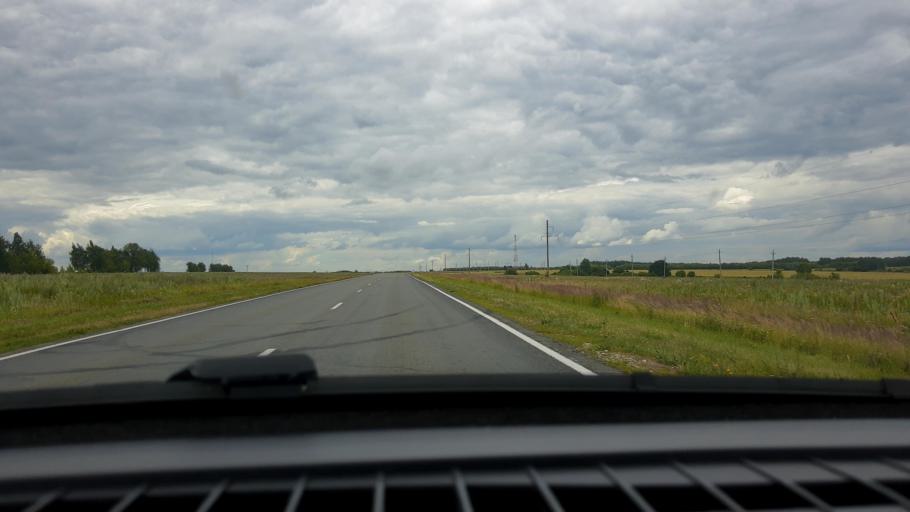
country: RU
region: Nizjnij Novgorod
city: Sergach
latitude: 55.5439
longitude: 45.5034
